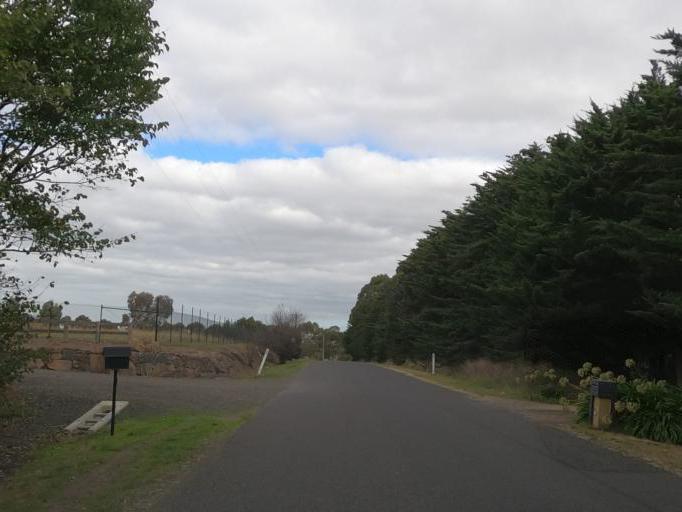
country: AU
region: Victoria
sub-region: Hume
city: Greenvale
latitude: -37.5596
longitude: 144.8698
